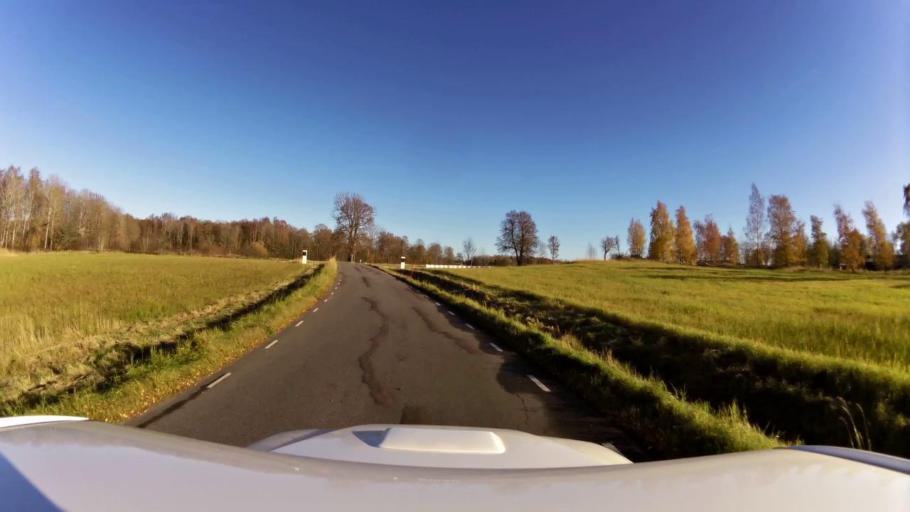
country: SE
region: OEstergoetland
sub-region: Linkopings Kommun
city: Sturefors
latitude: 58.2457
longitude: 15.6647
